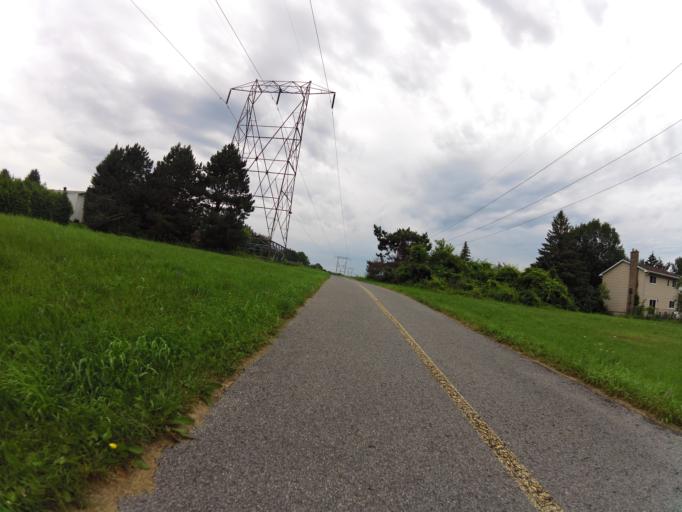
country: CA
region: Ontario
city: Bells Corners
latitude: 45.3292
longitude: -75.7713
